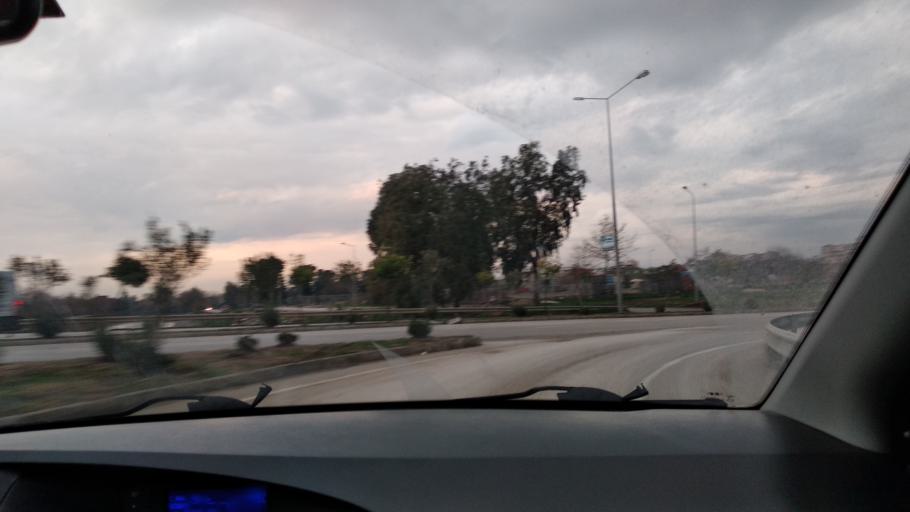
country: TR
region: Adana
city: Yuregir
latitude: 37.0094
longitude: 35.3912
